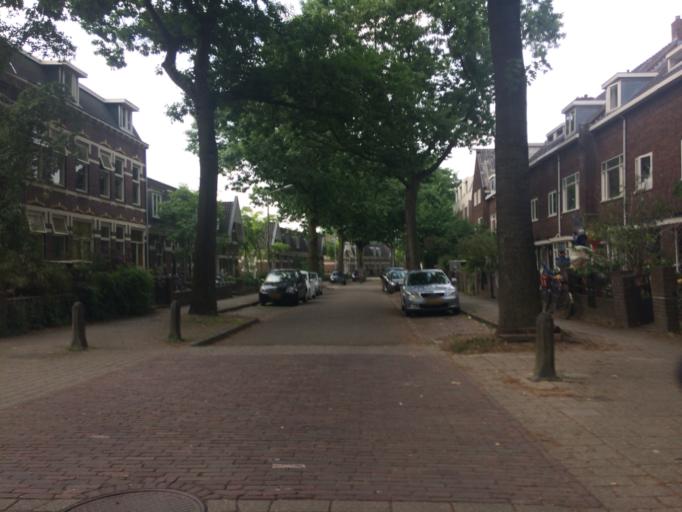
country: NL
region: Gelderland
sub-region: Gemeente Nijmegen
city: Nijmegen
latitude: 51.8394
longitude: 5.8709
